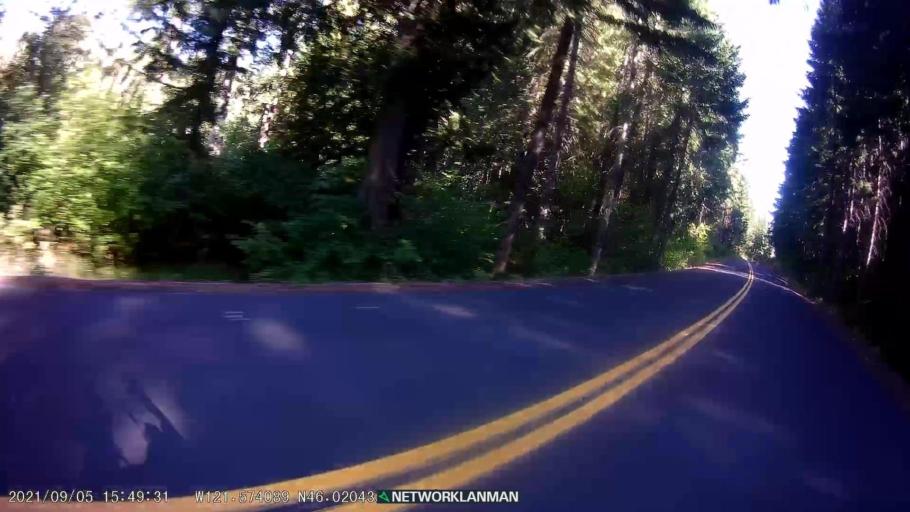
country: US
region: Washington
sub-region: Klickitat County
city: White Salmon
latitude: 46.0201
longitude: -121.5738
